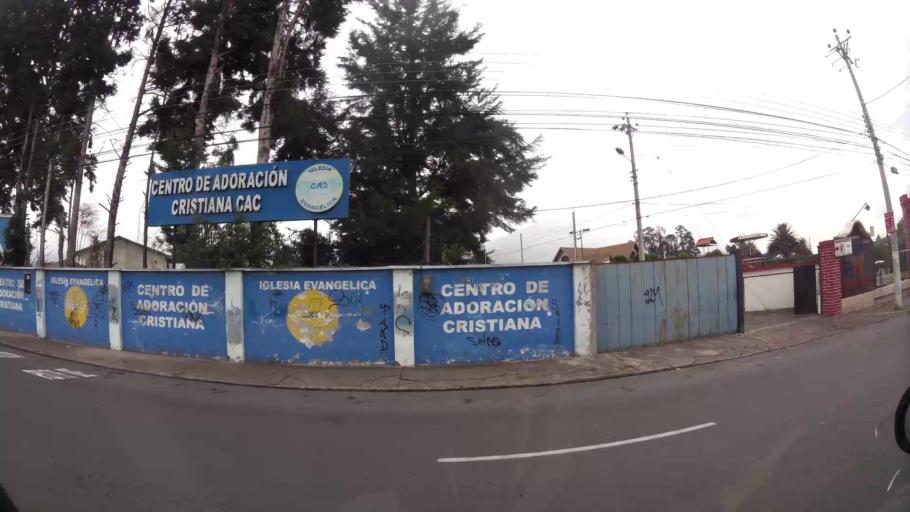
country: EC
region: Pichincha
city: Sangolqui
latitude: -0.3048
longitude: -78.4676
